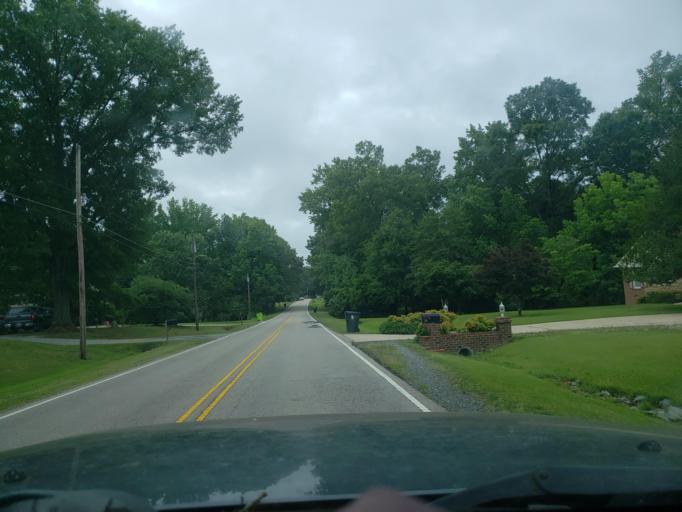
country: US
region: North Carolina
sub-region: Durham County
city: Gorman
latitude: 35.9728
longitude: -78.7847
